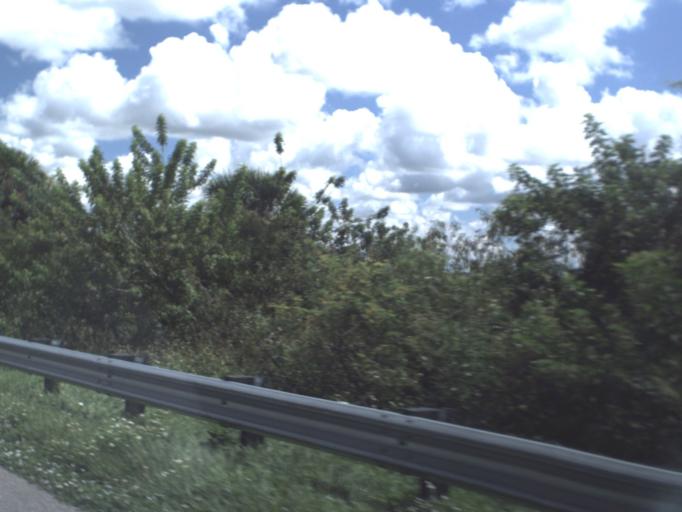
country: US
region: Florida
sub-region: Glades County
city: Buckhead Ridge
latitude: 27.2115
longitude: -81.1158
